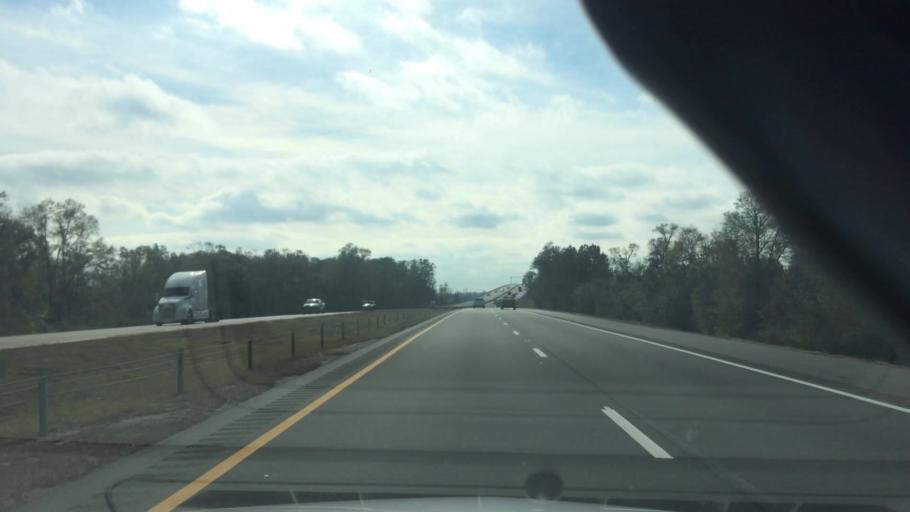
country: US
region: North Carolina
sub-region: New Hanover County
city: Wrightsboro
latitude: 34.3089
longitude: -77.9507
